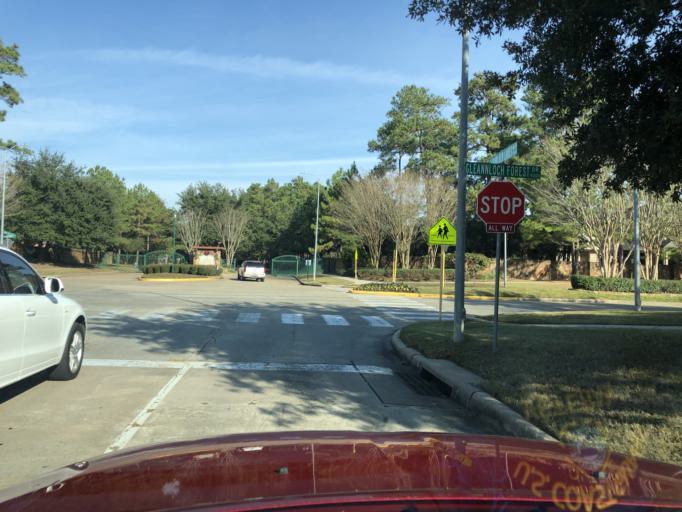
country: US
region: Texas
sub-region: Harris County
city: Tomball
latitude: 30.0330
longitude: -95.5672
